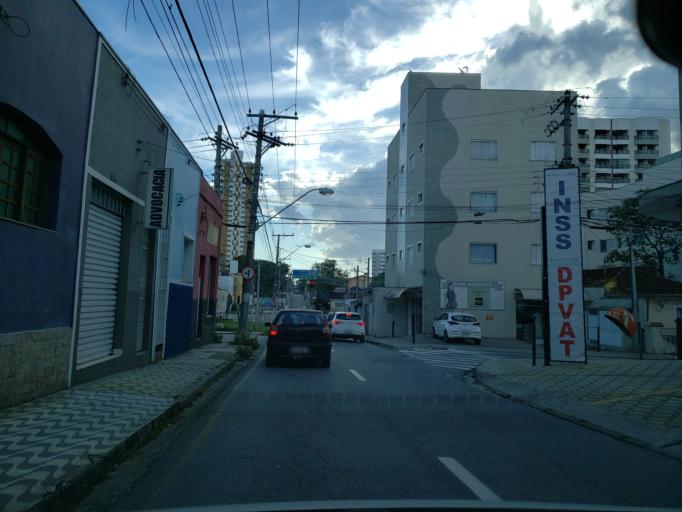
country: BR
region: Sao Paulo
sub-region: Taubate
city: Taubate
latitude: -23.0342
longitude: -45.5643
